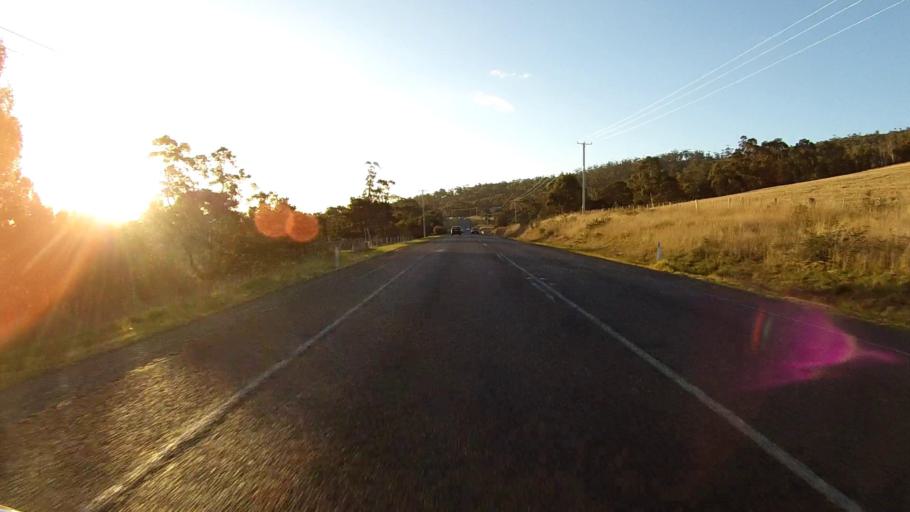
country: AU
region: Tasmania
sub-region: Sorell
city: Sorell
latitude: -42.7913
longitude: 147.6070
